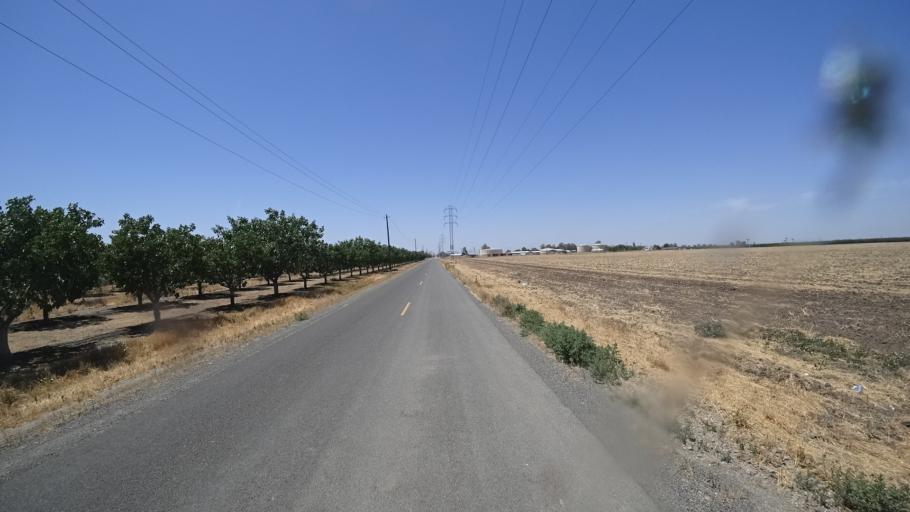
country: US
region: California
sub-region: Kings County
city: Corcoran
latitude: 36.1089
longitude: -119.5454
